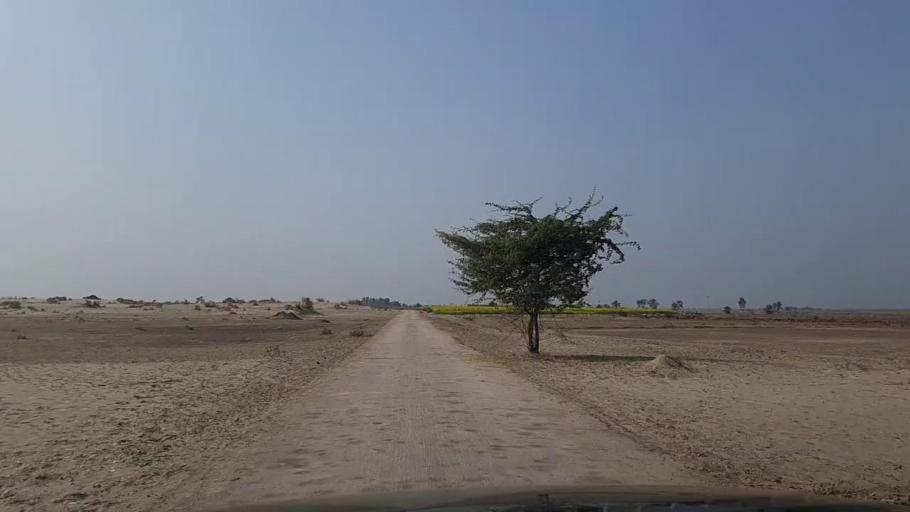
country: PK
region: Sindh
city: Daur
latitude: 26.3854
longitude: 68.4177
